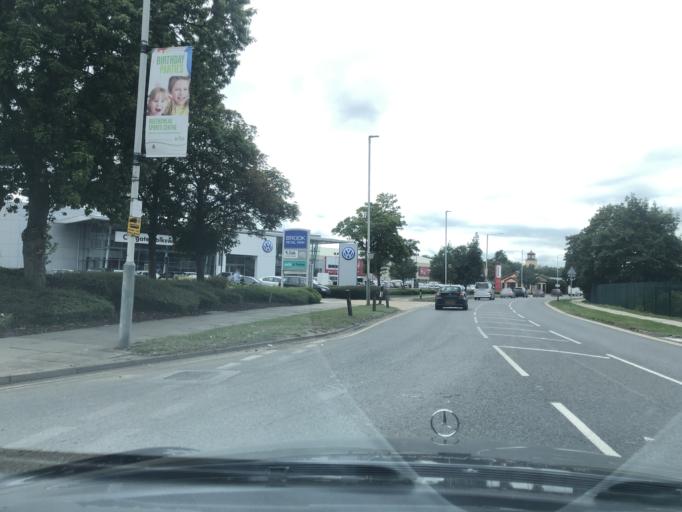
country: GB
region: England
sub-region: Greater London
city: Northolt
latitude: 51.5565
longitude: -0.3898
